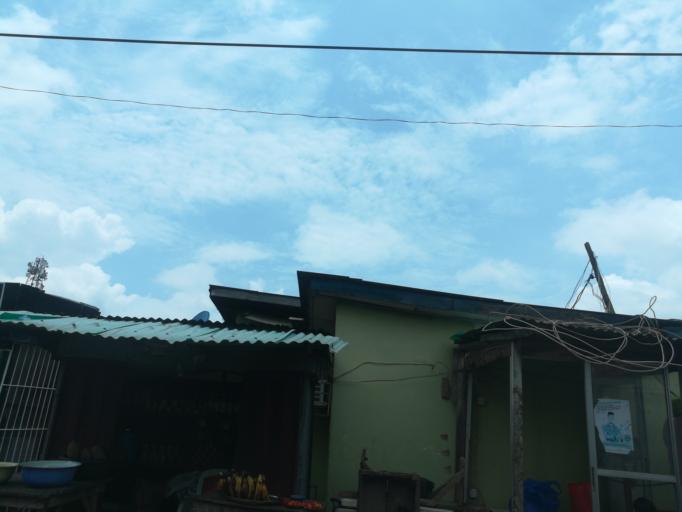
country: NG
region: Lagos
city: Ikeja
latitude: 6.5939
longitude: 3.3603
